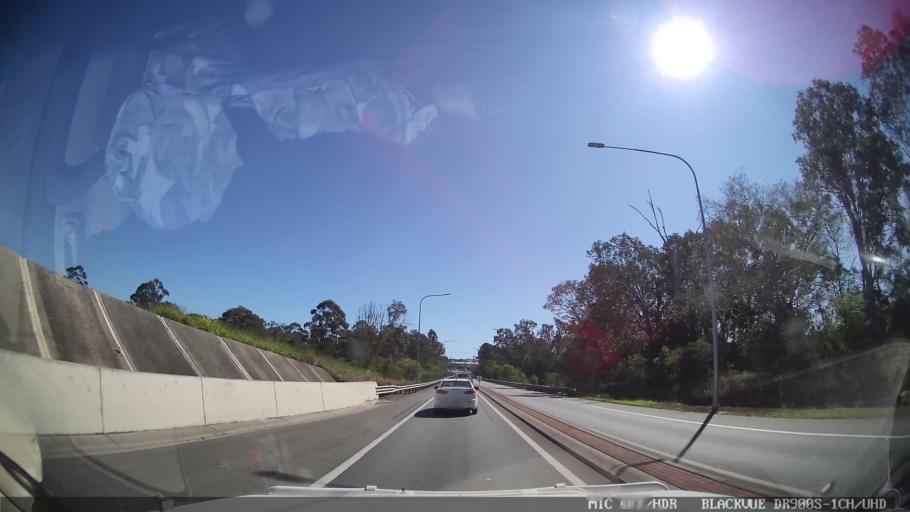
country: AU
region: Queensland
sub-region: Gympie Regional Council
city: Monkland
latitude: -26.2349
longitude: 152.6985
